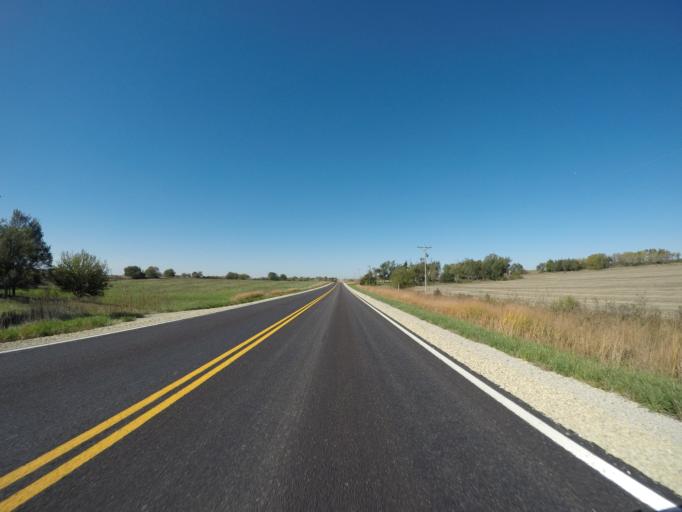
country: US
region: Kansas
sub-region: Clay County
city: Clay Center
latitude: 39.3140
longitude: -96.9541
